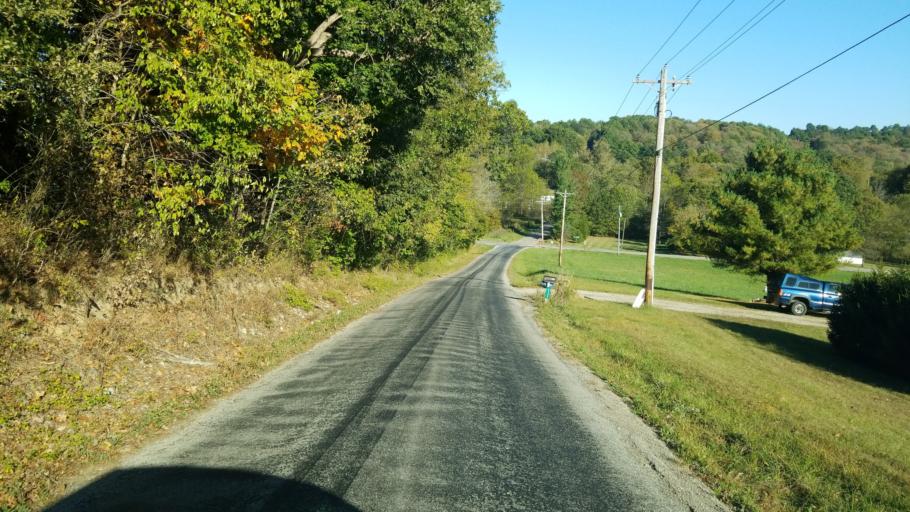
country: US
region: Ohio
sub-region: Licking County
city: Utica
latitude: 40.1752
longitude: -82.3819
